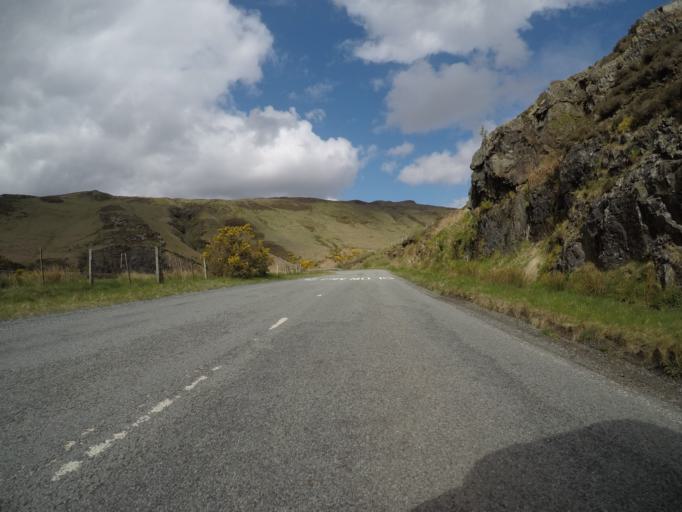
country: GB
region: Scotland
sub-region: Highland
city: Isle of Skye
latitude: 57.3039
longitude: -6.2995
